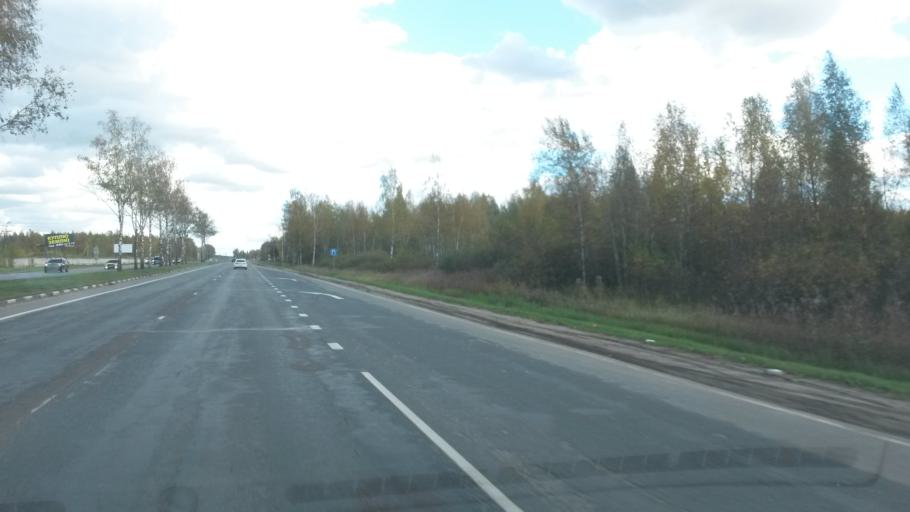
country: RU
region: Jaroslavl
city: Yaroslavl
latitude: 57.5409
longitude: 39.9799
